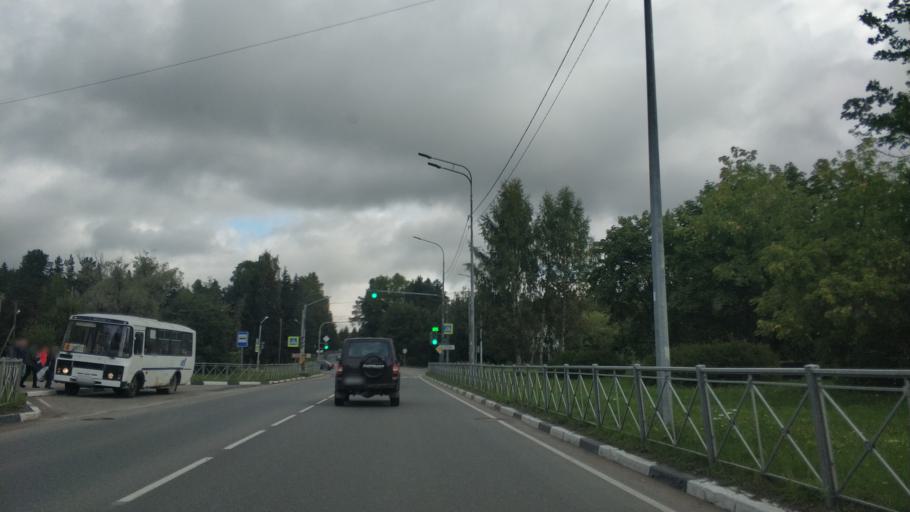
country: RU
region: Republic of Karelia
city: Sortavala
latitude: 61.7114
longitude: 30.6991
